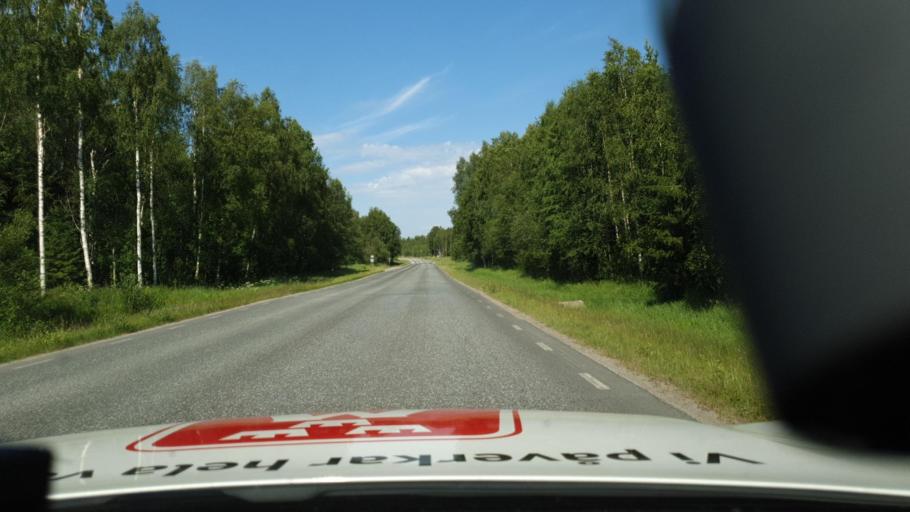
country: SE
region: Norrbotten
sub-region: Kalix Kommun
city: Rolfs
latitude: 65.8689
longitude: 23.1163
